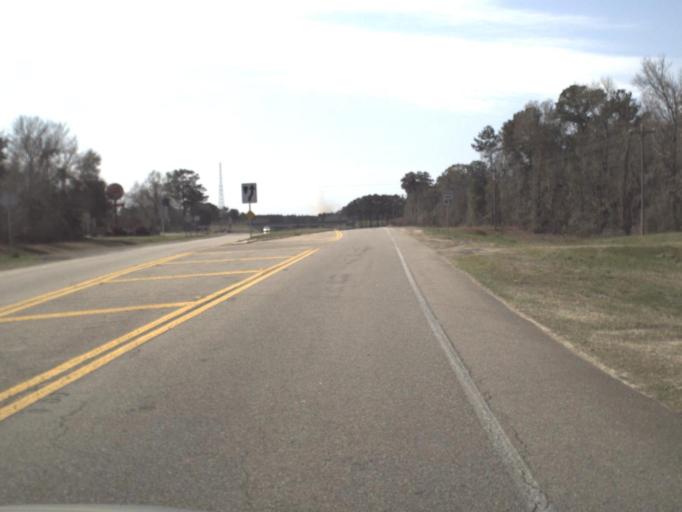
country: US
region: Florida
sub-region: Gadsden County
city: Gretna
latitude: 30.5832
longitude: -84.6959
